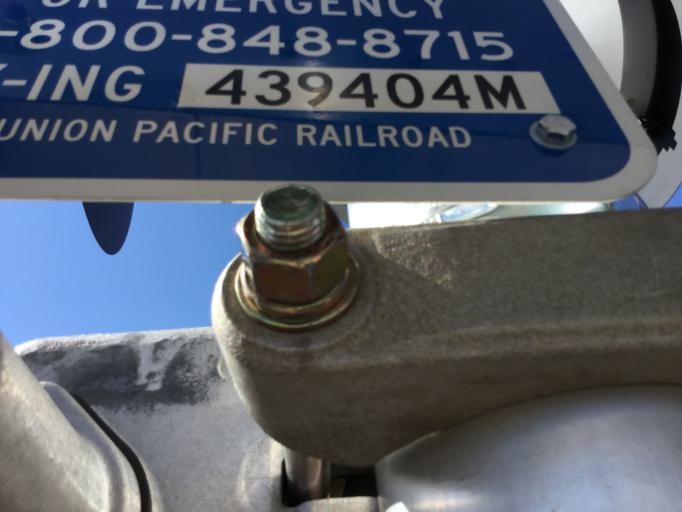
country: US
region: Kansas
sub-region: Anderson County
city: Garnett
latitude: 38.3536
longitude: -95.1554
